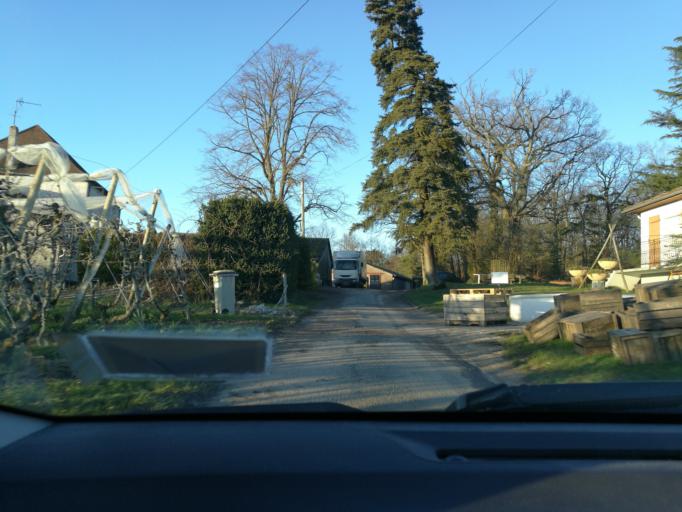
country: FR
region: Centre
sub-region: Departement du Loiret
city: Semoy
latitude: 47.9406
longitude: 1.9649
